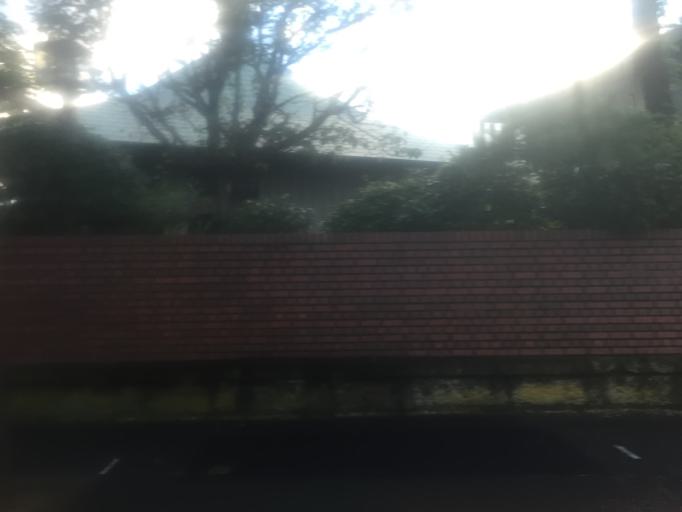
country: JP
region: Tokyo
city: Tokyo
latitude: 35.5993
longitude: 139.6644
